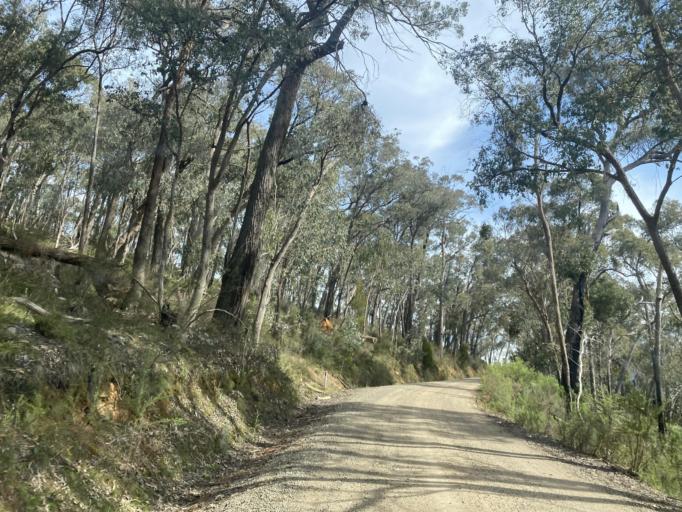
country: AU
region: Victoria
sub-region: Mansfield
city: Mansfield
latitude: -36.8302
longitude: 146.1649
